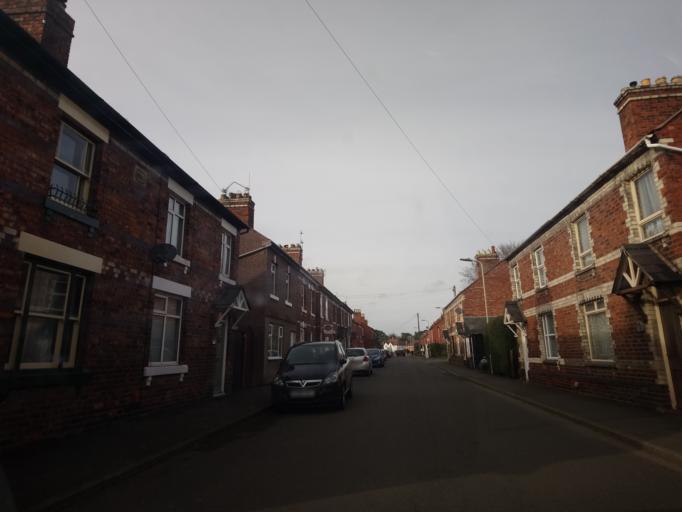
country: GB
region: England
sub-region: Shropshire
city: Wem
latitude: 52.8579
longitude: -2.7172
